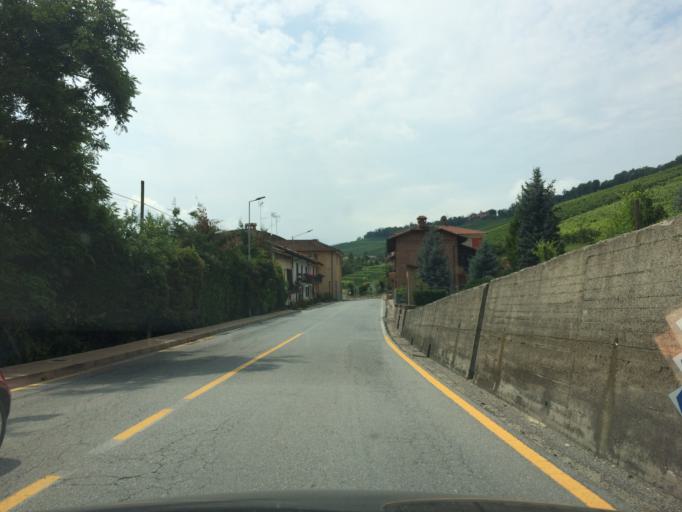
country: IT
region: Piedmont
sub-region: Provincia di Cuneo
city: Barolo
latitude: 44.6126
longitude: 7.9408
